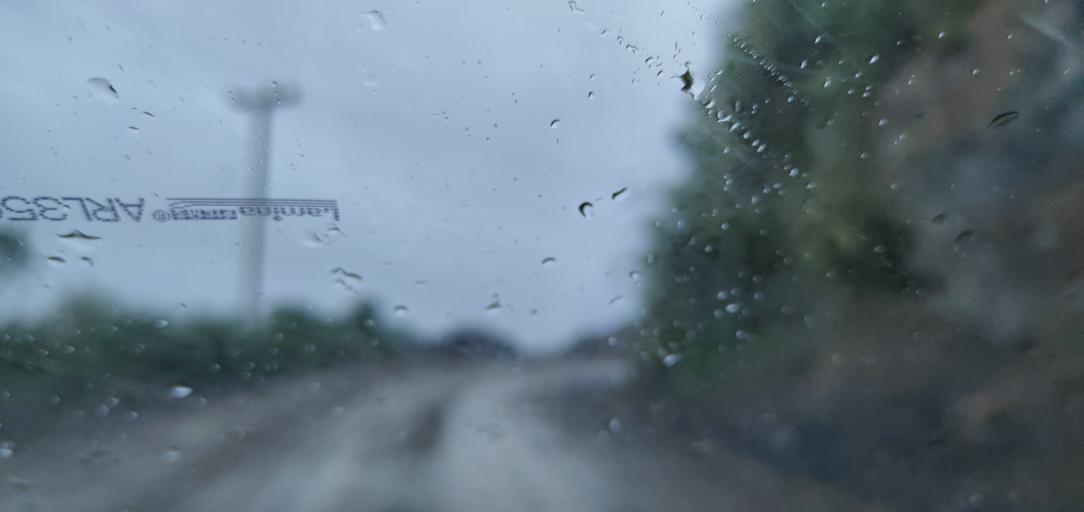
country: LA
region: Phongsali
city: Phongsali
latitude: 21.4291
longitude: 102.1632
